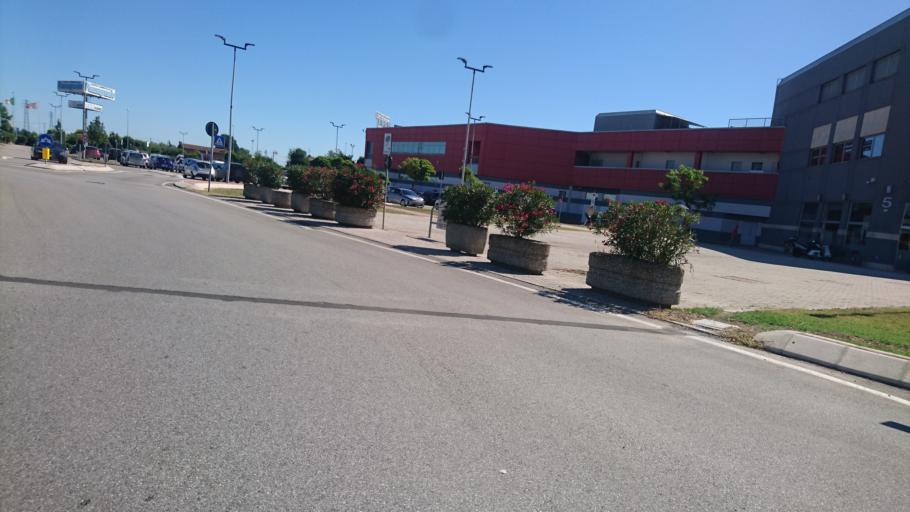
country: IT
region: Veneto
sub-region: Provincia di Padova
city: Sant'Angelo di Piove di Sacco
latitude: 45.3045
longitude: 12.0203
